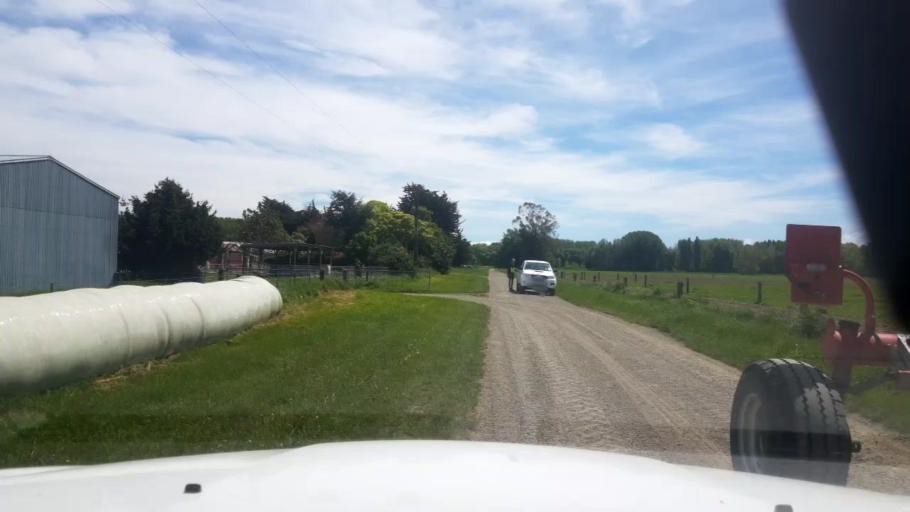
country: NZ
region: Canterbury
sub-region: Timaru District
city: Pleasant Point
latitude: -44.2622
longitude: 171.0944
